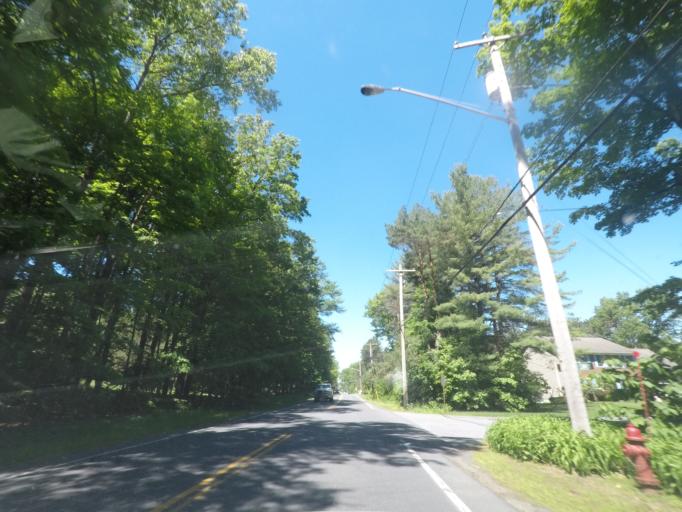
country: US
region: New York
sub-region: Saratoga County
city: Country Knolls
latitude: 42.8580
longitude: -73.8116
